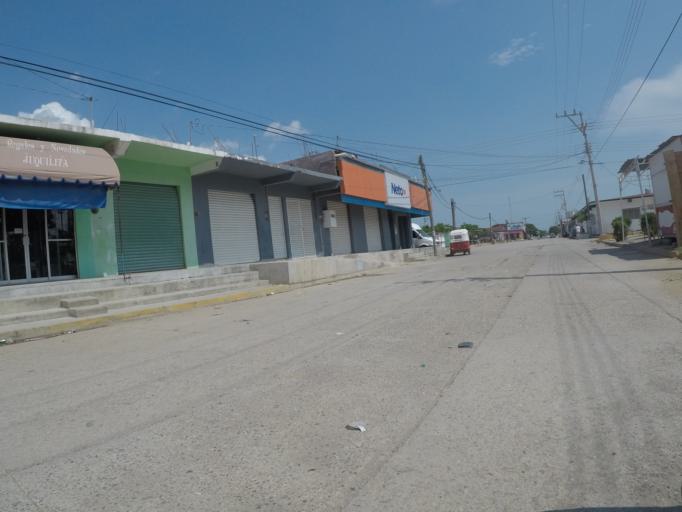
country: MX
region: Oaxaca
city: Union Hidalgo
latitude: 16.4738
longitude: -94.8299
